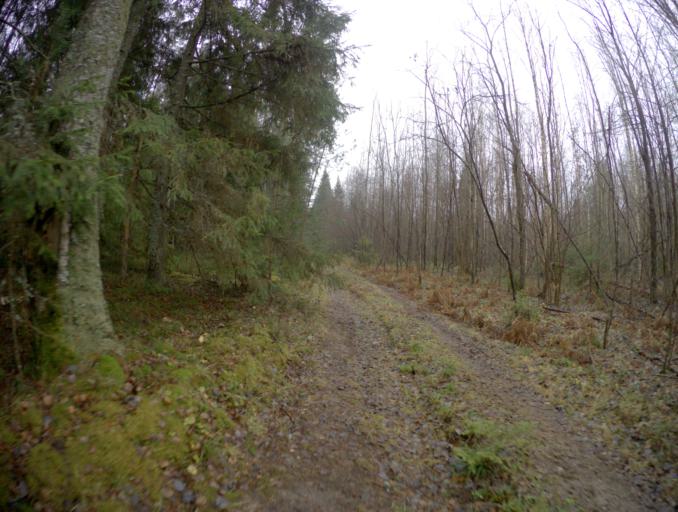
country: RU
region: Vladimir
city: Golovino
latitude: 56.0099
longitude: 40.4841
